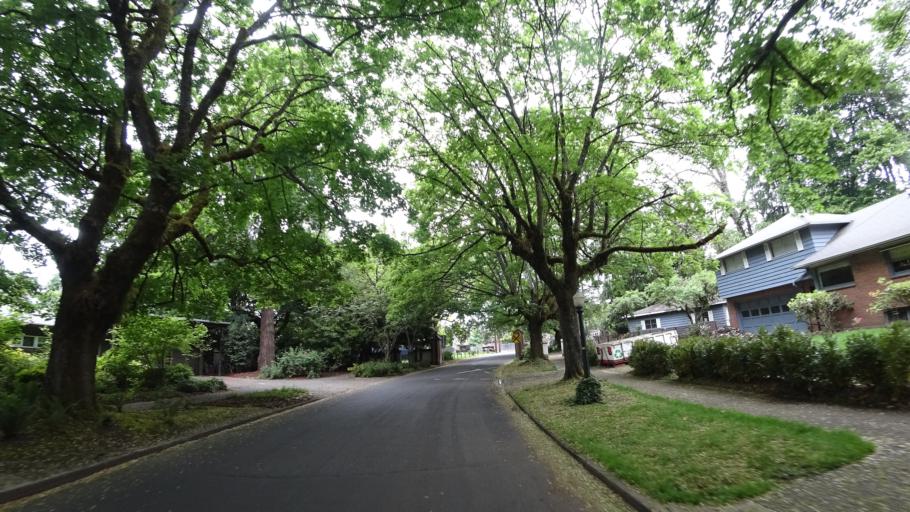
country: US
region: Oregon
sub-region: Clackamas County
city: Milwaukie
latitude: 45.4579
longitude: -122.6524
